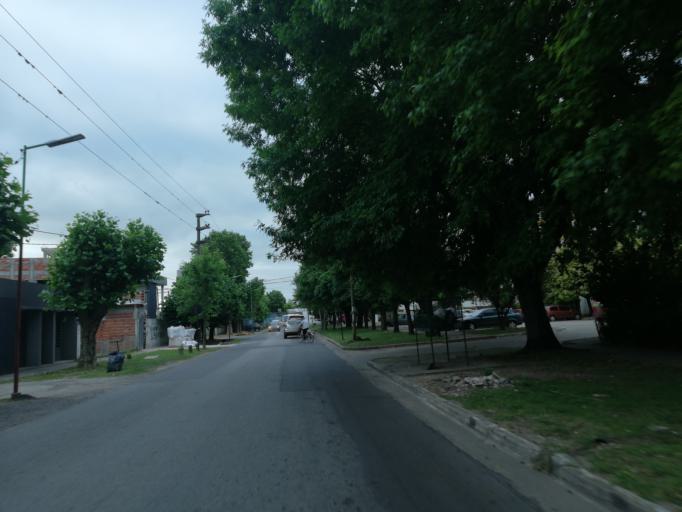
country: AR
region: Buenos Aires
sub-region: Partido de La Plata
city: La Plata
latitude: -34.8498
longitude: -58.0779
